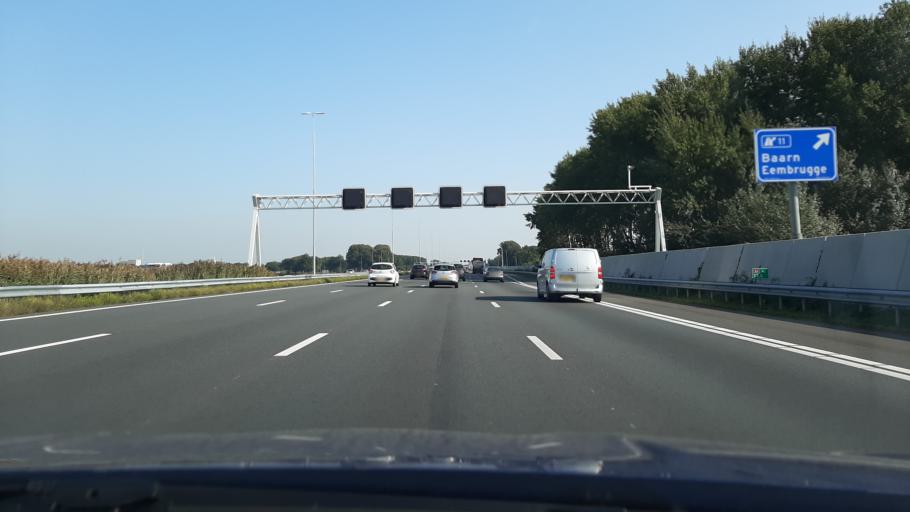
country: NL
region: Utrecht
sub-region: Gemeente Baarn
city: Baarn
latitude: 52.2215
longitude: 5.2913
